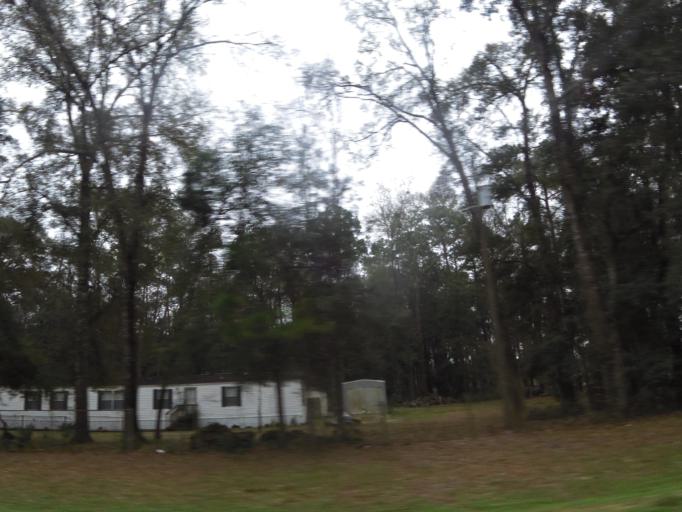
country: US
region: Florida
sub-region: Alachua County
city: High Springs
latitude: 29.8576
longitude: -82.5685
